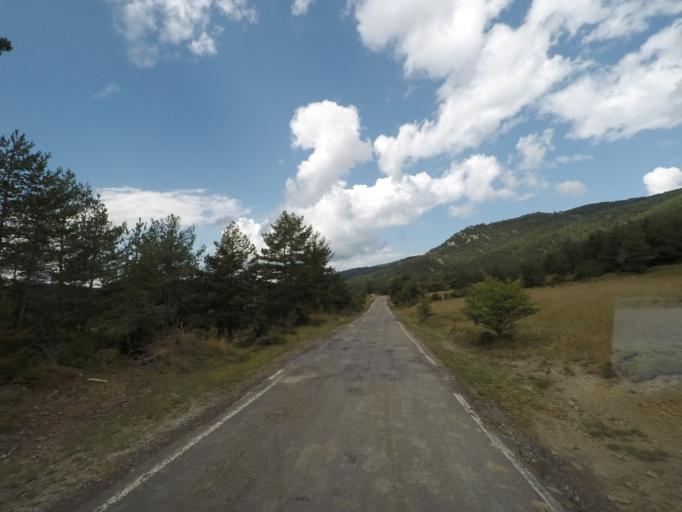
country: ES
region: Aragon
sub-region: Provincia de Huesca
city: Fiscal
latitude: 42.4011
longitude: -0.0536
